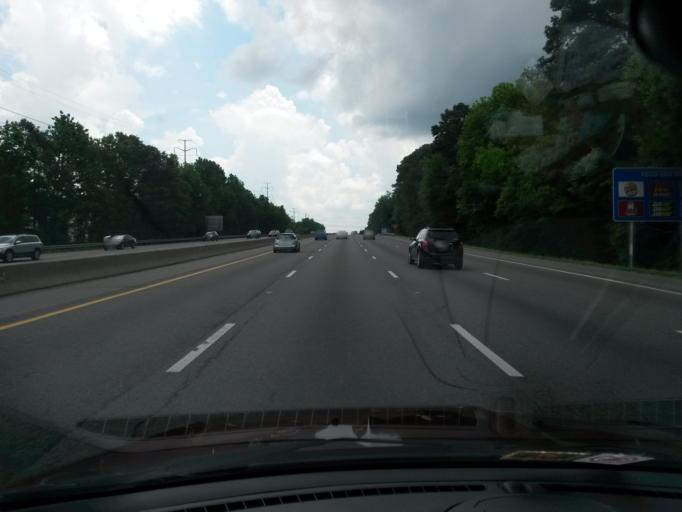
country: US
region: Virginia
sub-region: Chesterfield County
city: Bellwood
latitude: 37.4222
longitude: -77.4283
